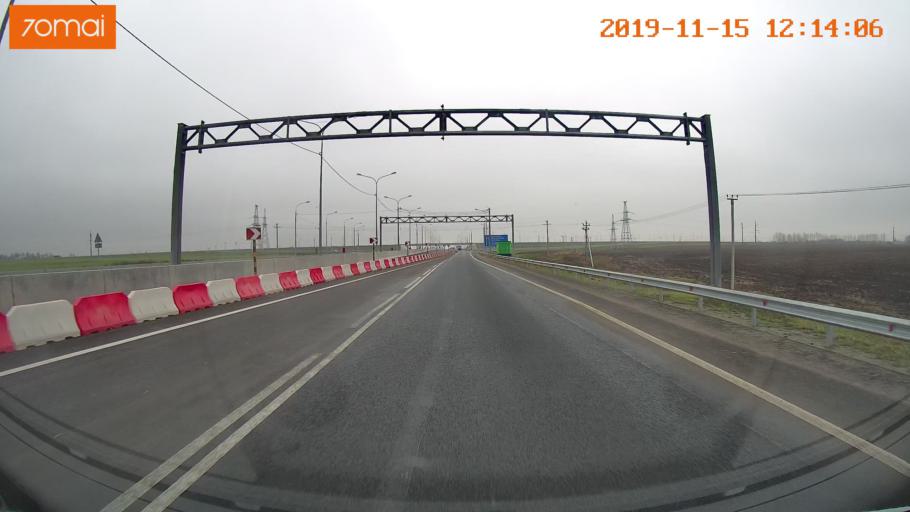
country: RU
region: Vologda
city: Vologda
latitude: 59.1606
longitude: 39.8028
